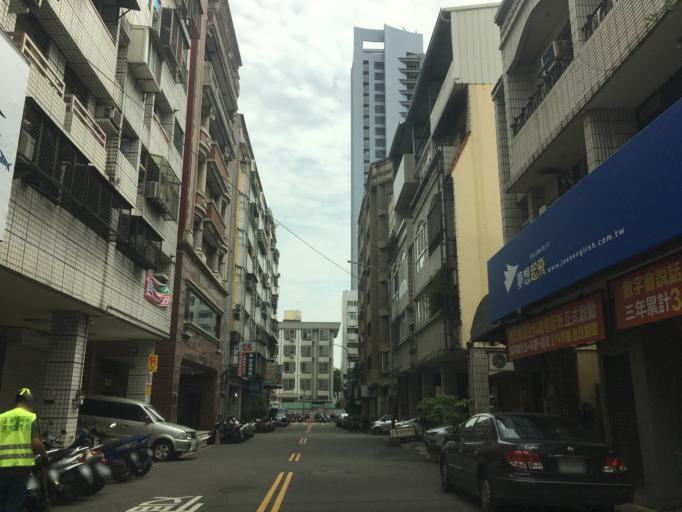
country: TW
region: Taiwan
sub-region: Taichung City
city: Taichung
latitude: 24.1419
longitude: 120.6488
